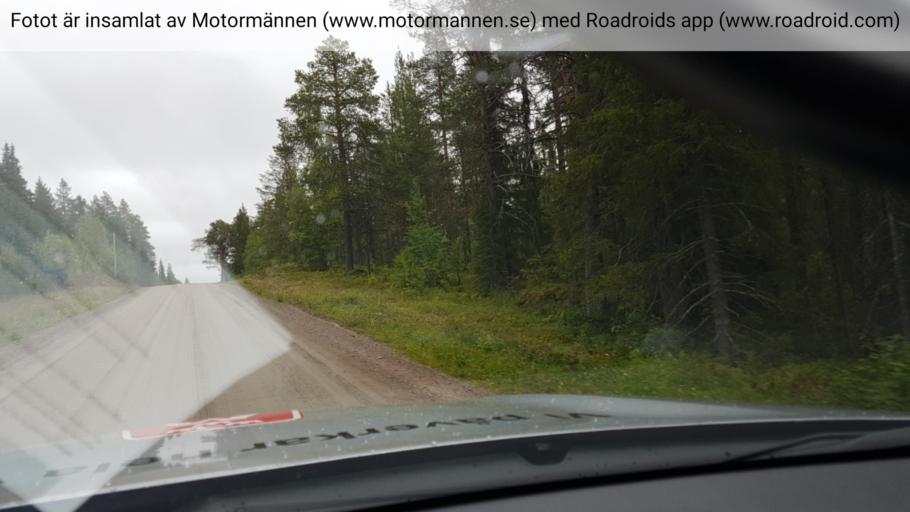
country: SE
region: Norrbotten
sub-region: Gallivare Kommun
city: Gaellivare
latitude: 66.7059
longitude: 20.4434
